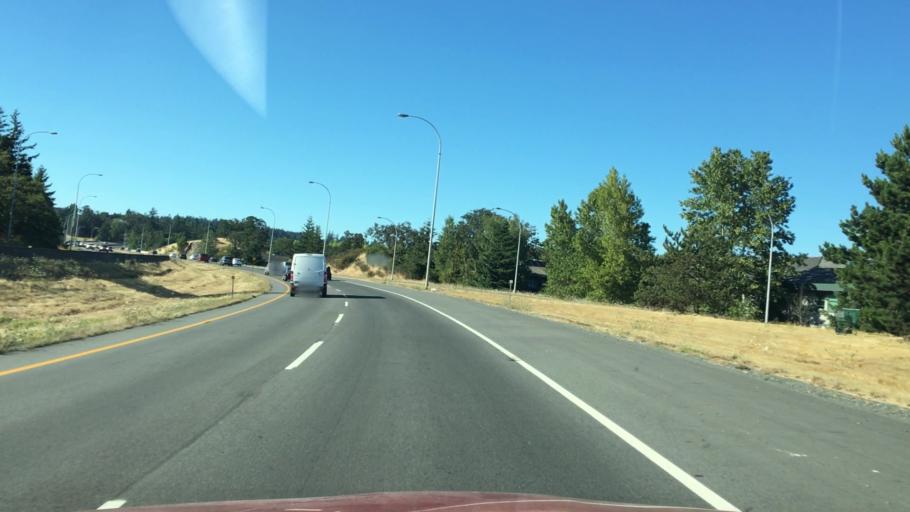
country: CA
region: British Columbia
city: Victoria
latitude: 48.4876
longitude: -123.3844
